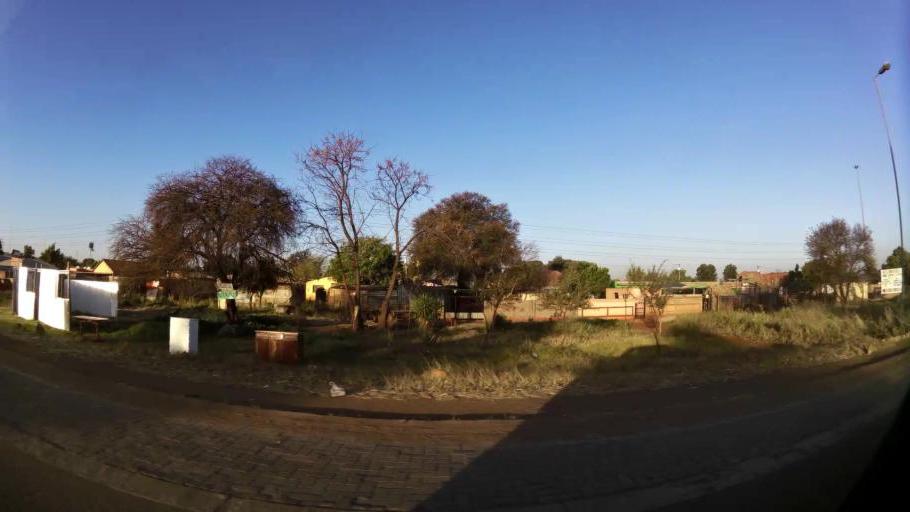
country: ZA
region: North-West
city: Ga-Rankuwa
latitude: -25.5827
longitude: 28.0743
